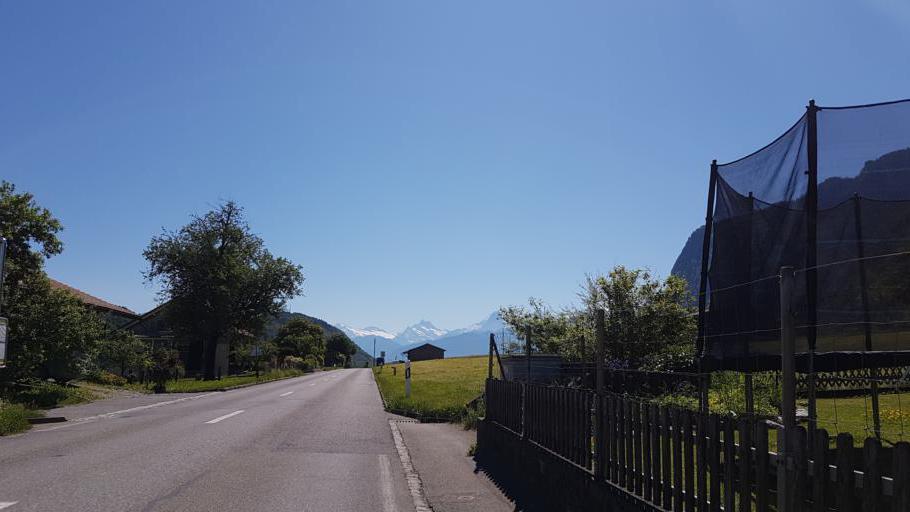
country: CH
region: Bern
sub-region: Thun District
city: Thierachern
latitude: 46.7145
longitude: 7.5624
